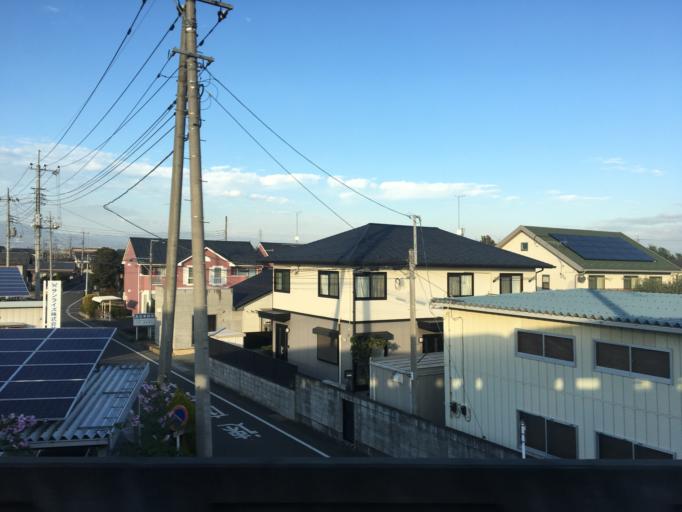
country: JP
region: Gunma
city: Isesaki
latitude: 36.3301
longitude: 139.1853
